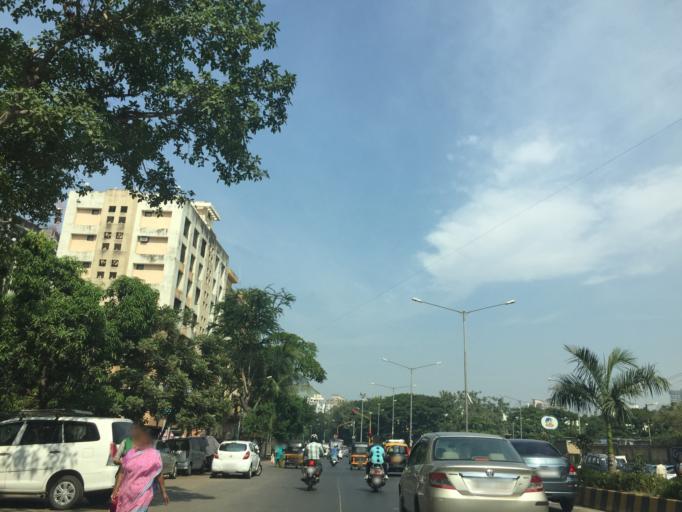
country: IN
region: Maharashtra
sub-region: Mumbai Suburban
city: Borivli
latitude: 19.2287
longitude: 72.8409
